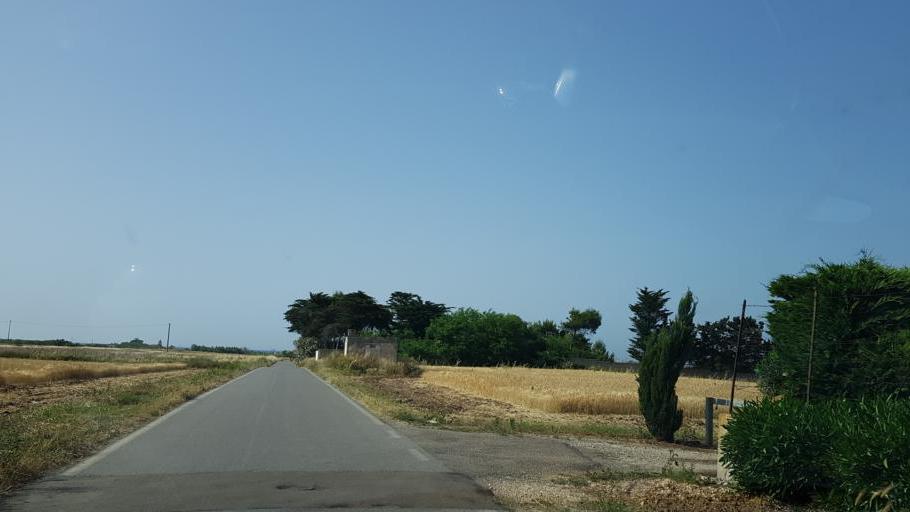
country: IT
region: Apulia
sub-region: Provincia di Brindisi
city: Brindisi
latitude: 40.6785
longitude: 17.8870
